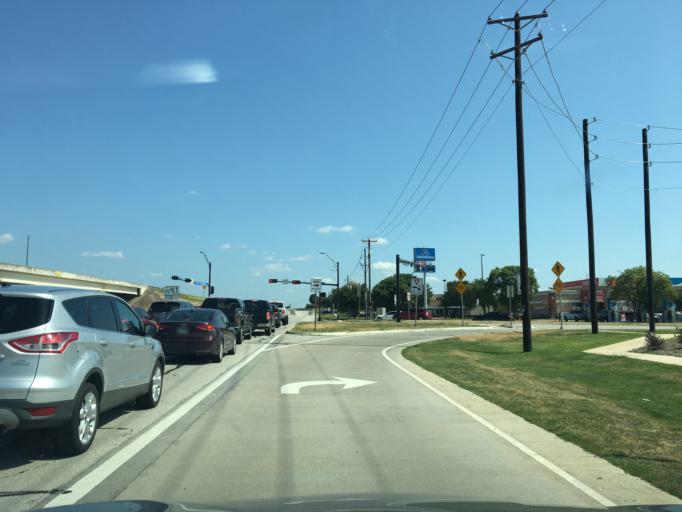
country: US
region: Texas
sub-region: Tarrant County
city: Kennedale
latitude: 32.6468
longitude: -97.1862
